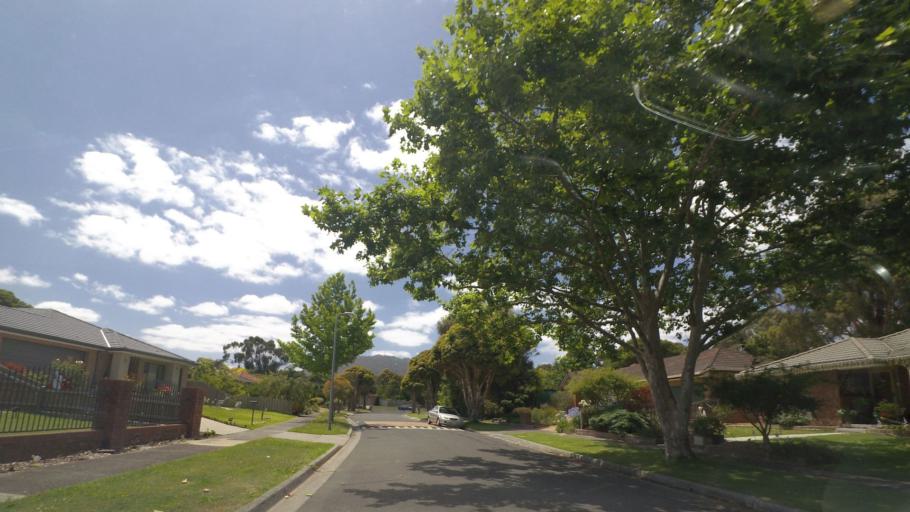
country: AU
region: Victoria
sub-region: Maroondah
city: Bayswater North
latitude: -37.8271
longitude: 145.3047
